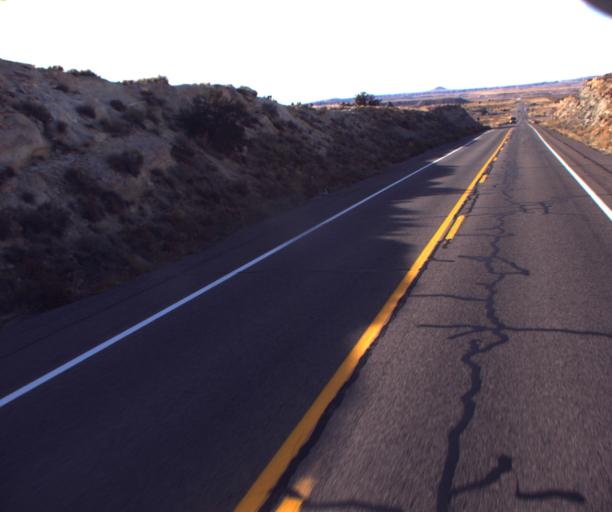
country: US
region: New Mexico
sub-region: San Juan County
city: Shiprock
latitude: 36.9164
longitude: -109.0792
